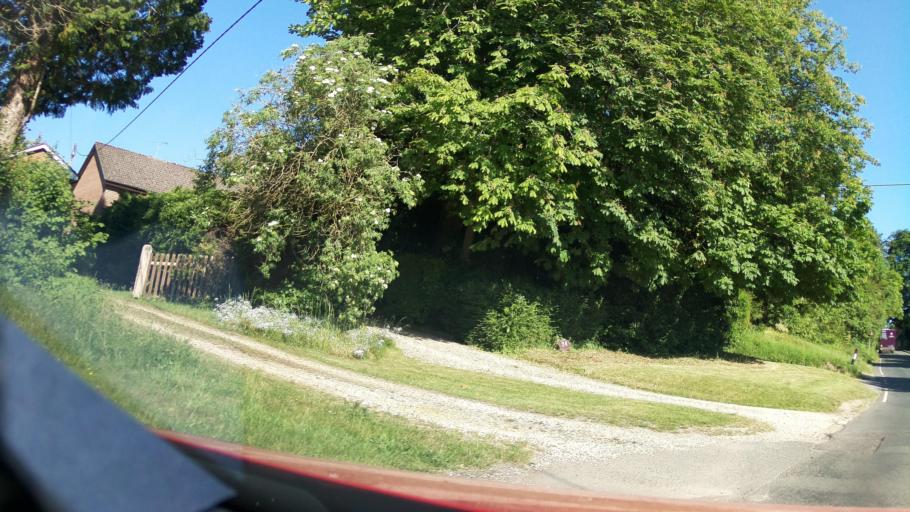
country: GB
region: England
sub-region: Hampshire
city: Winchester
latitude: 51.0858
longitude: -1.3483
